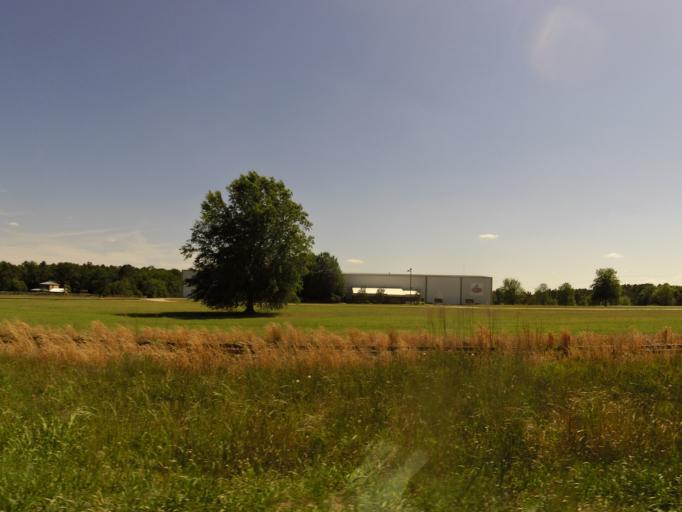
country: US
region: South Carolina
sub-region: Aiken County
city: Aiken
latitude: 33.5229
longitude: -81.6145
